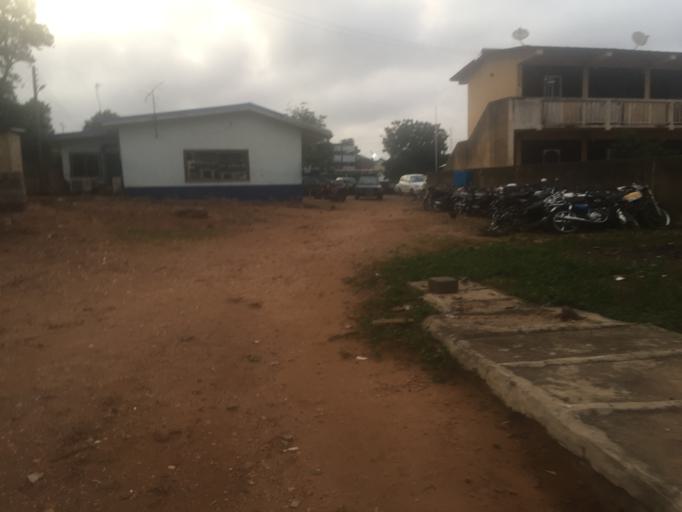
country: GH
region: Greater Accra
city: Dome
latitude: 5.6042
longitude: -0.2249
